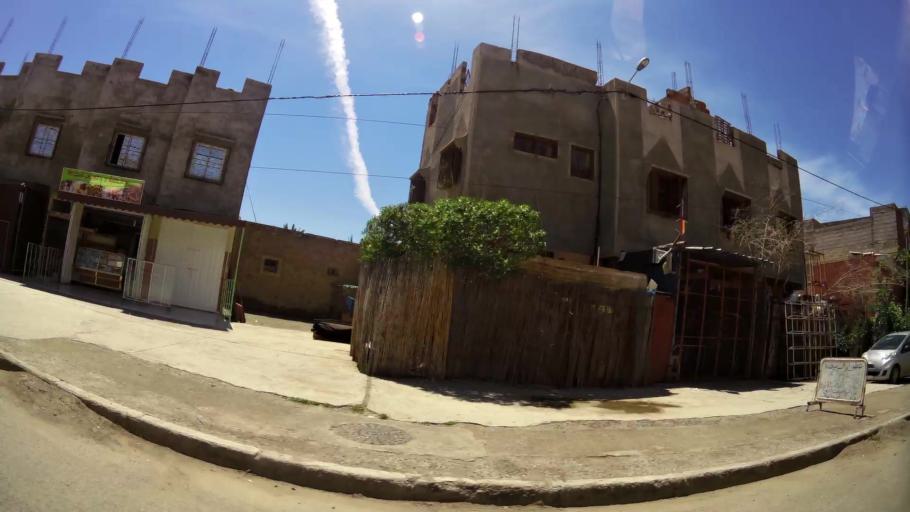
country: MA
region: Marrakech-Tensift-Al Haouz
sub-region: Marrakech
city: Marrakesh
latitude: 31.6368
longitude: -8.0454
